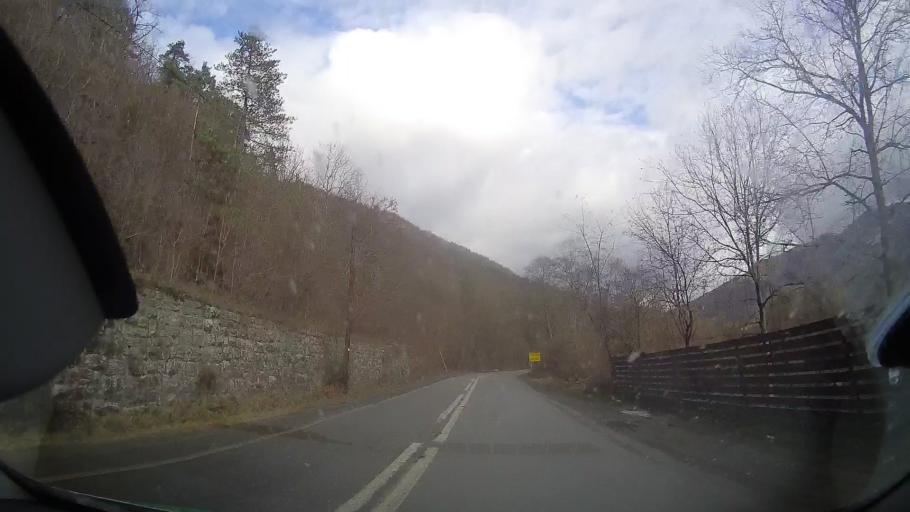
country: RO
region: Alba
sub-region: Comuna Ocolis
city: Ocolis
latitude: 46.4815
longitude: 23.5093
